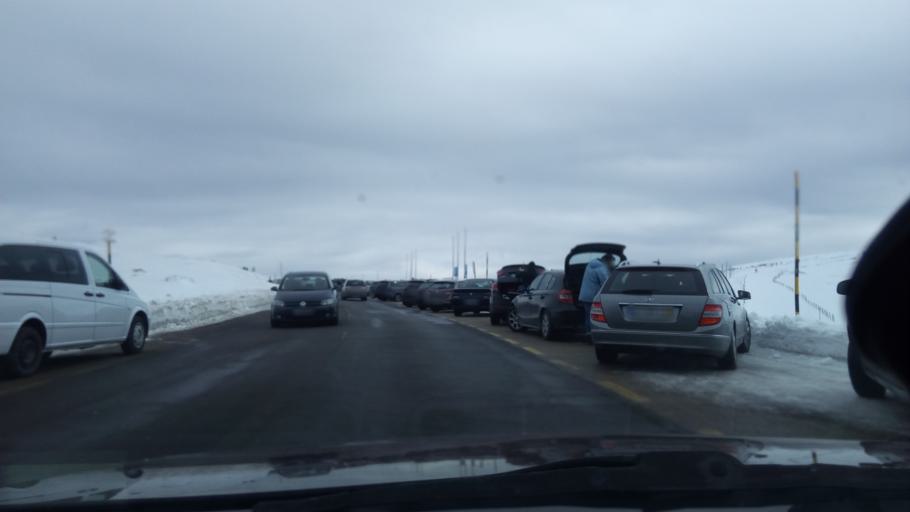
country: PT
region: Guarda
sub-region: Manteigas
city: Manteigas
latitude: 40.3308
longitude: -7.6153
